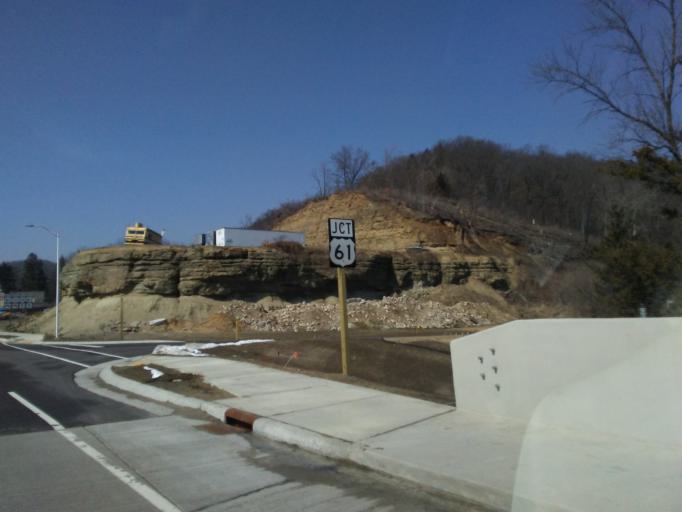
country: US
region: Wisconsin
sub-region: Vernon County
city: Viroqua
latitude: 43.4446
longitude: -90.7644
